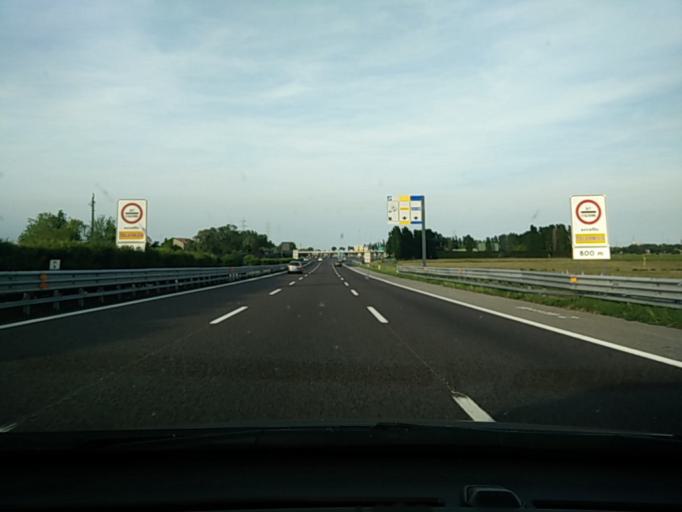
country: IT
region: Veneto
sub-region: Provincia di Venezia
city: Fornase
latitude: 45.4688
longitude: 12.1851
